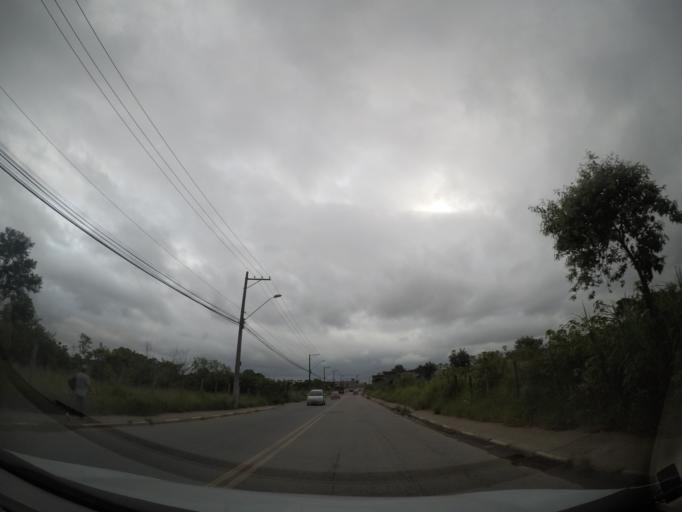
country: BR
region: Sao Paulo
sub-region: Guarulhos
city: Guarulhos
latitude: -23.4089
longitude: -46.4427
